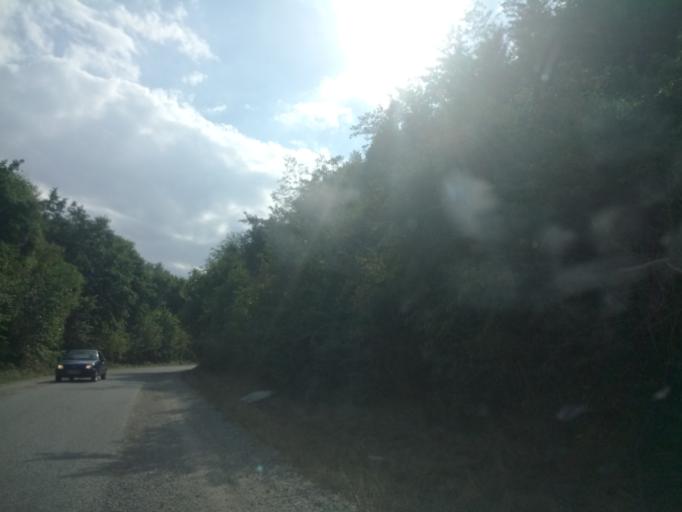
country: RS
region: Autonomna Pokrajina Vojvodina
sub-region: Sremski Okrug
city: Irig
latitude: 45.1029
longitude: 19.9036
